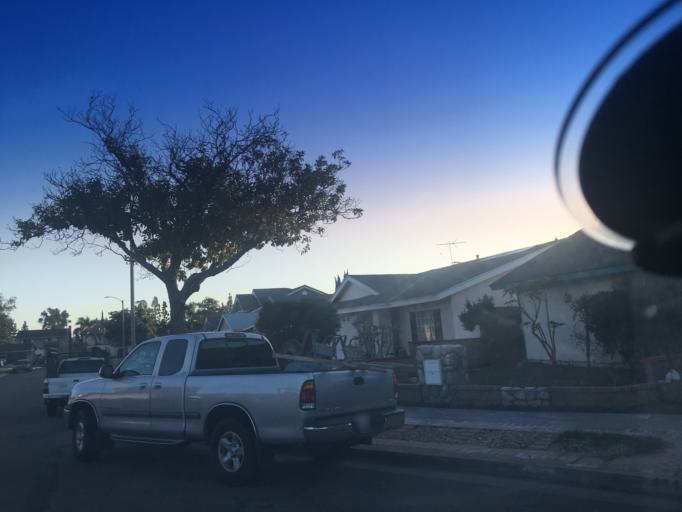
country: US
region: California
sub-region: Orange County
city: Anaheim
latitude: 33.8214
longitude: -117.8830
